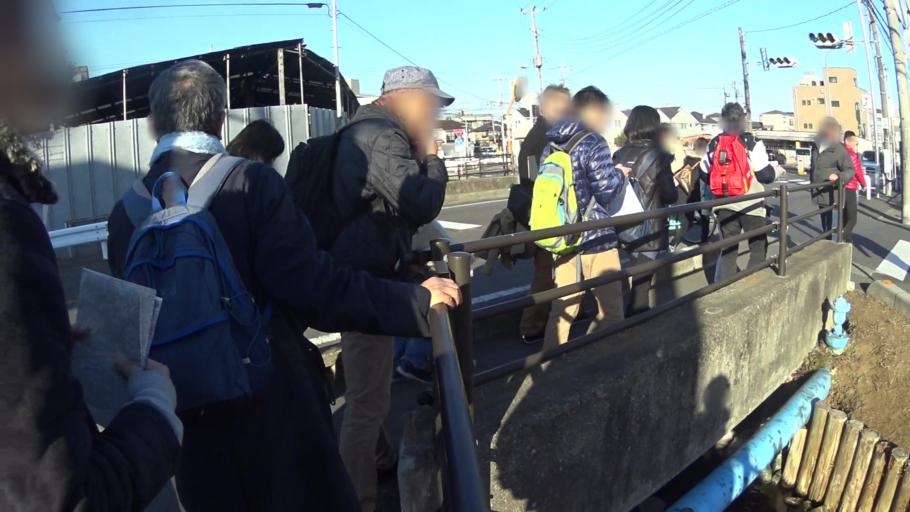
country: JP
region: Saitama
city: Shimotoda
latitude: 35.8479
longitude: 139.6930
